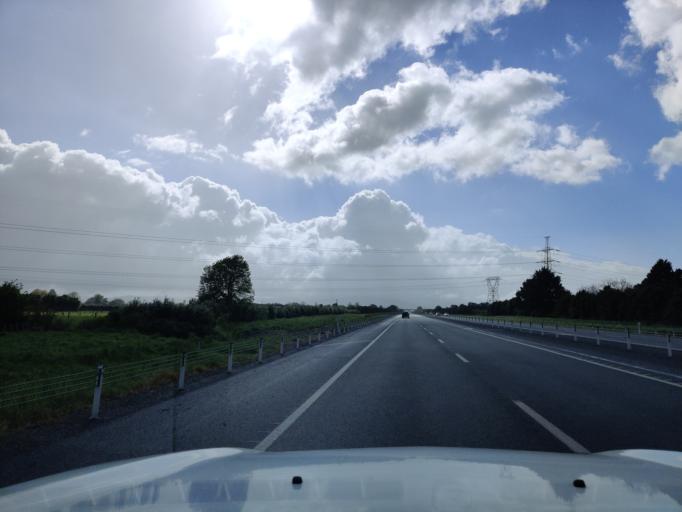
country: NZ
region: Waikato
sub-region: Waipa District
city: Cambridge
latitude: -37.8685
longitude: 175.4210
